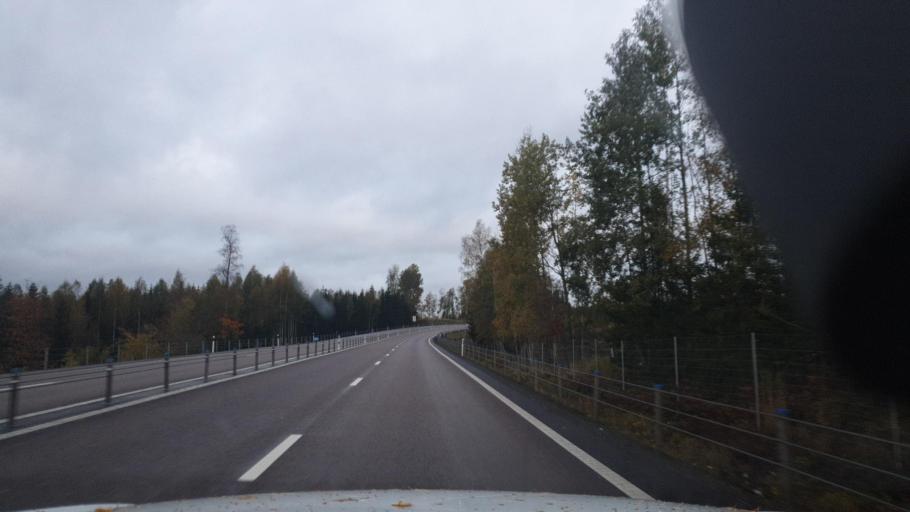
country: SE
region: Vaermland
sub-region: Eda Kommun
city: Amotfors
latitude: 59.7591
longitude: 12.4089
